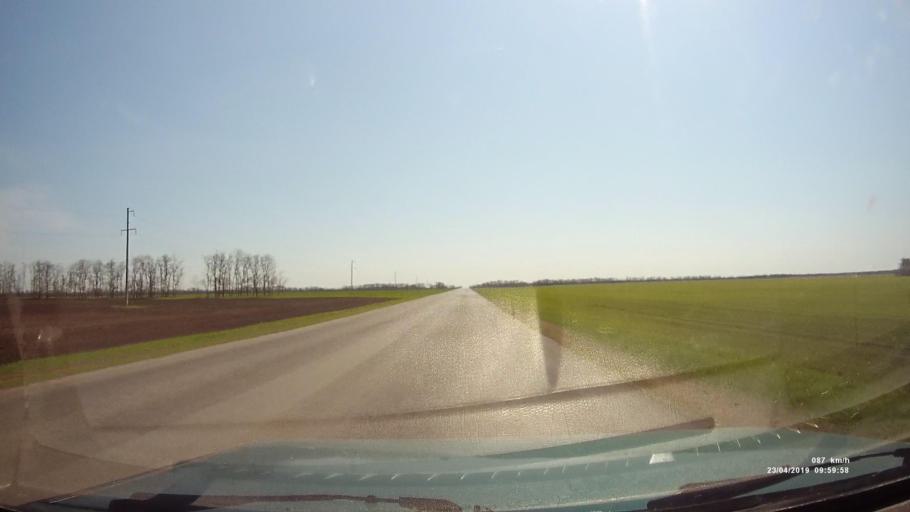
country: RU
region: Rostov
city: Sovetskoye
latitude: 46.7727
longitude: 42.1228
